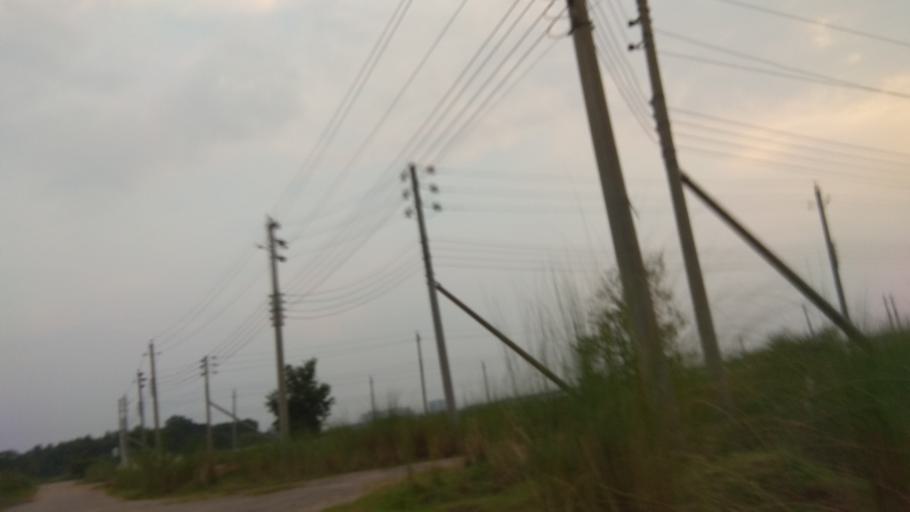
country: BD
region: Dhaka
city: Tungi
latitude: 23.8544
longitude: 90.3686
